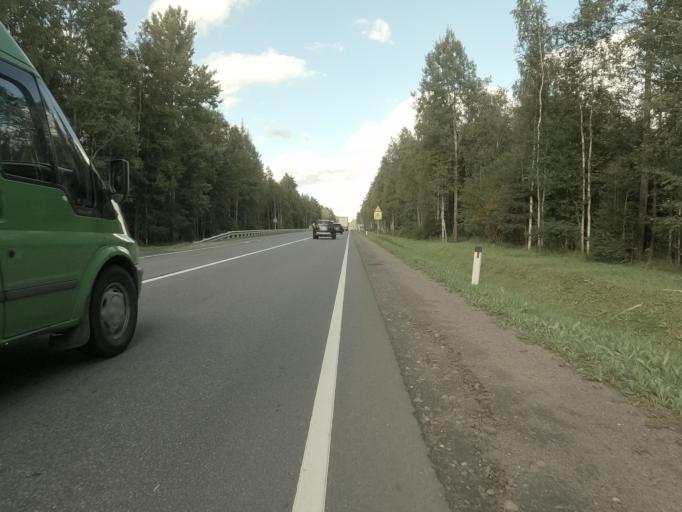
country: RU
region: Leningrad
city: Mga
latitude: 59.7054
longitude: 31.0109
